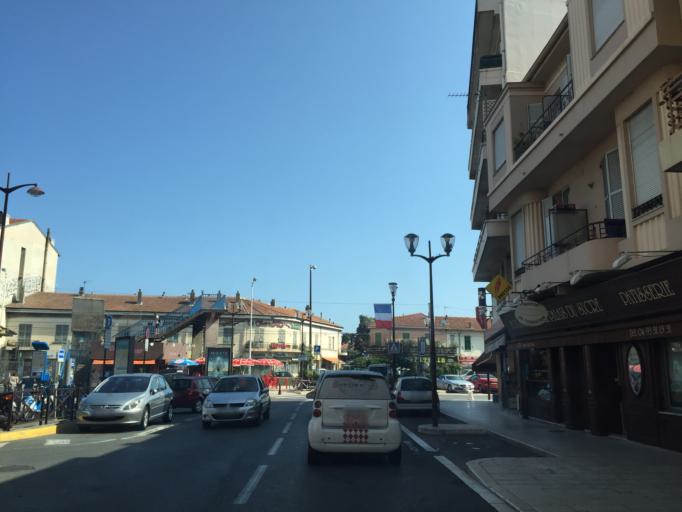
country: FR
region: Provence-Alpes-Cote d'Azur
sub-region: Departement des Alpes-Maritimes
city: Saint-Laurent-du-Var
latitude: 43.6627
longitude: 7.1940
